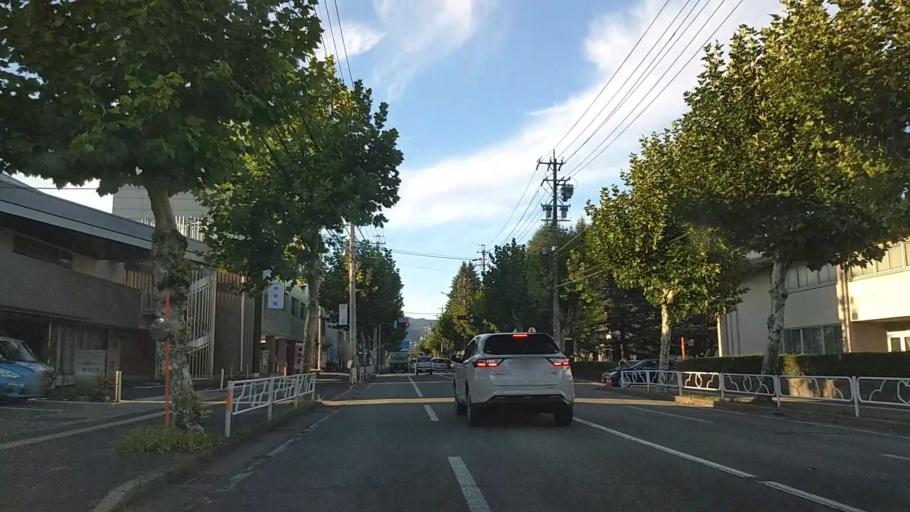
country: JP
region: Nagano
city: Nagano-shi
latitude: 36.6386
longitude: 138.1994
